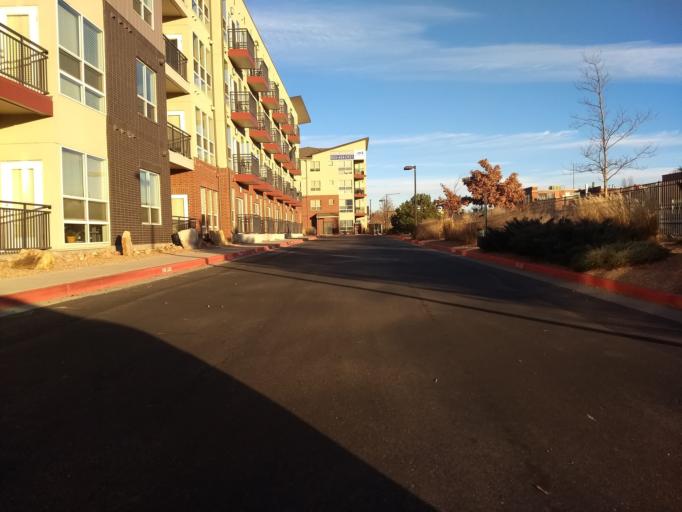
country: US
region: Colorado
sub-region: Denver County
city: Denver
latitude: 39.7114
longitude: -104.9942
